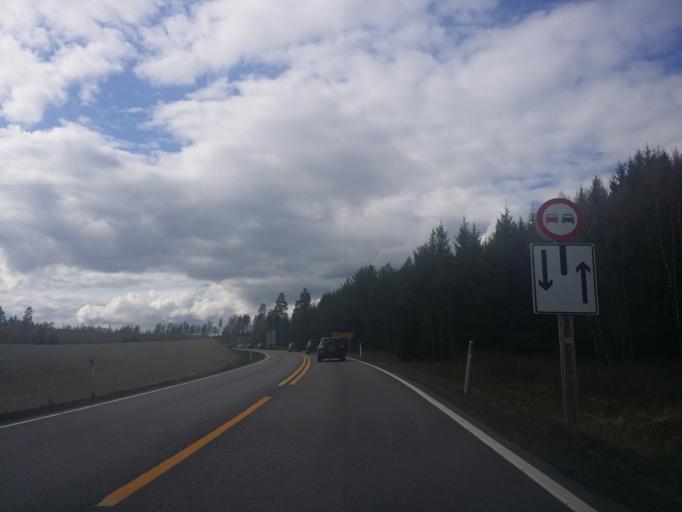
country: NO
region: Buskerud
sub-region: Ringerike
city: Honefoss
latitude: 60.1482
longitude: 10.2266
